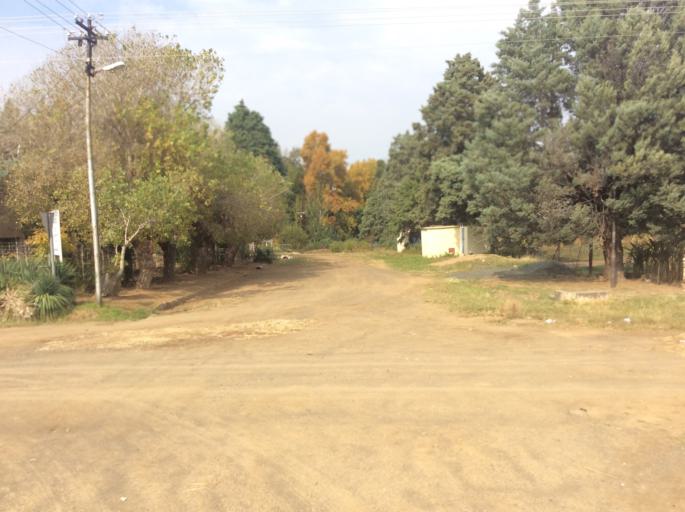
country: LS
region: Mafeteng
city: Mafeteng
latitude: -29.7252
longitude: 27.0368
